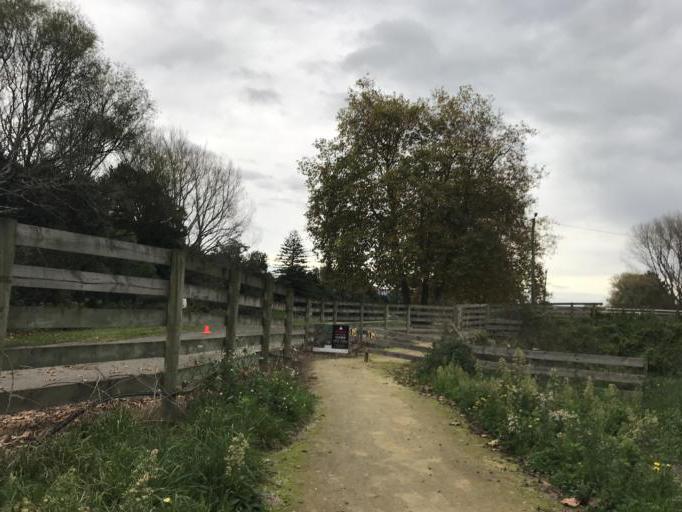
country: NZ
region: Manawatu-Wanganui
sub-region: Palmerston North City
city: Palmerston North
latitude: -40.3808
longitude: 175.5738
